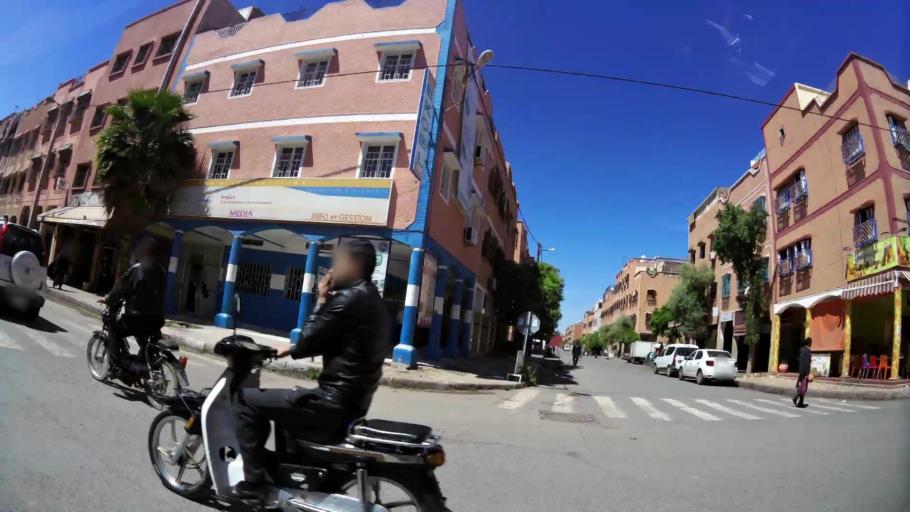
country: MA
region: Marrakech-Tensift-Al Haouz
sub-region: Marrakech
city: Marrakesh
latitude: 31.6316
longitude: -8.0667
